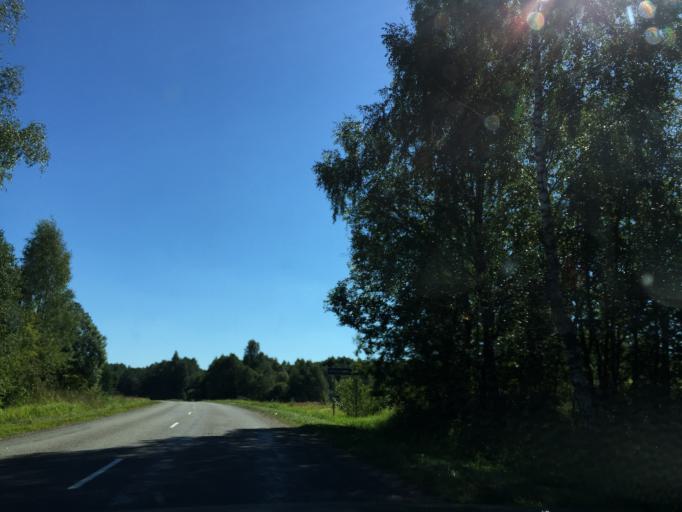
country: LV
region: Akniste
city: Akniste
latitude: 56.1212
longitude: 25.8310
